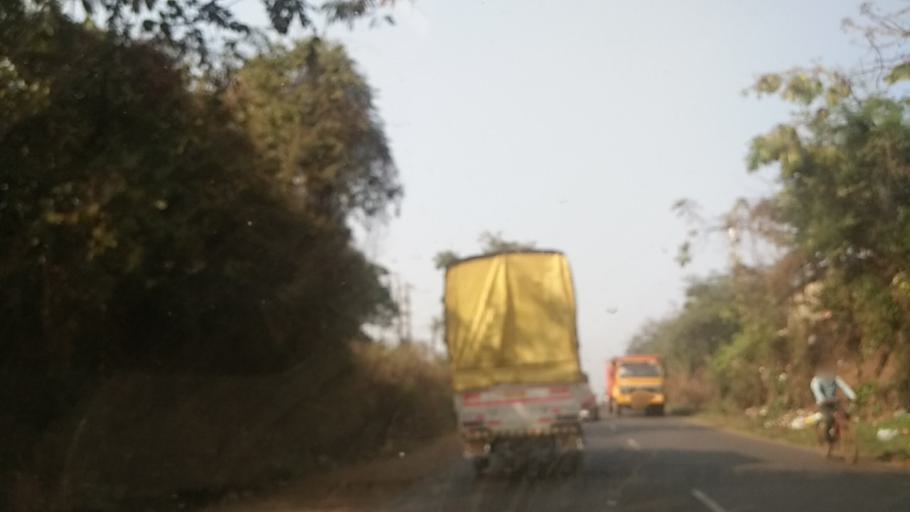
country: IN
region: Goa
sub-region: North Goa
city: Colovale
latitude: 15.6125
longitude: 73.8230
